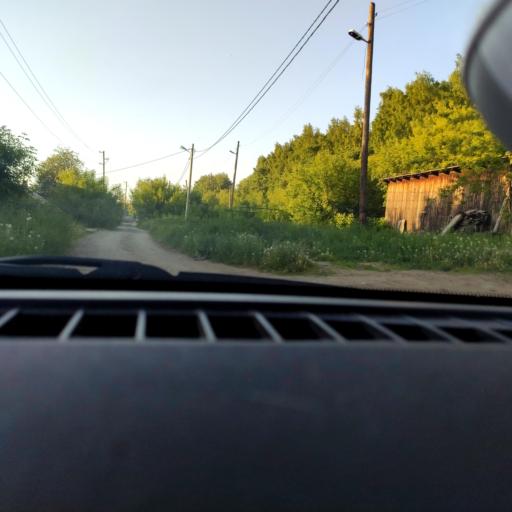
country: RU
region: Perm
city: Polazna
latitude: 58.1377
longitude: 56.3801
